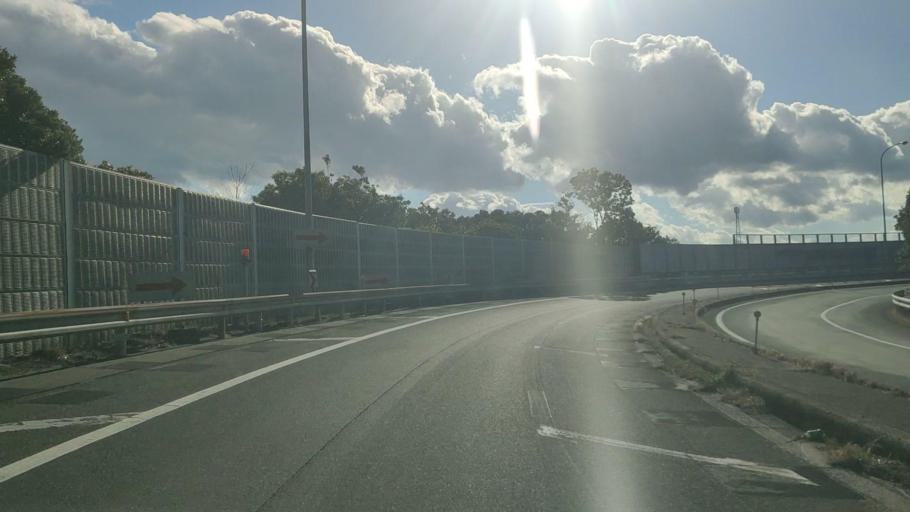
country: JP
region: Fukuoka
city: Nogata
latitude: 33.7796
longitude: 130.7423
